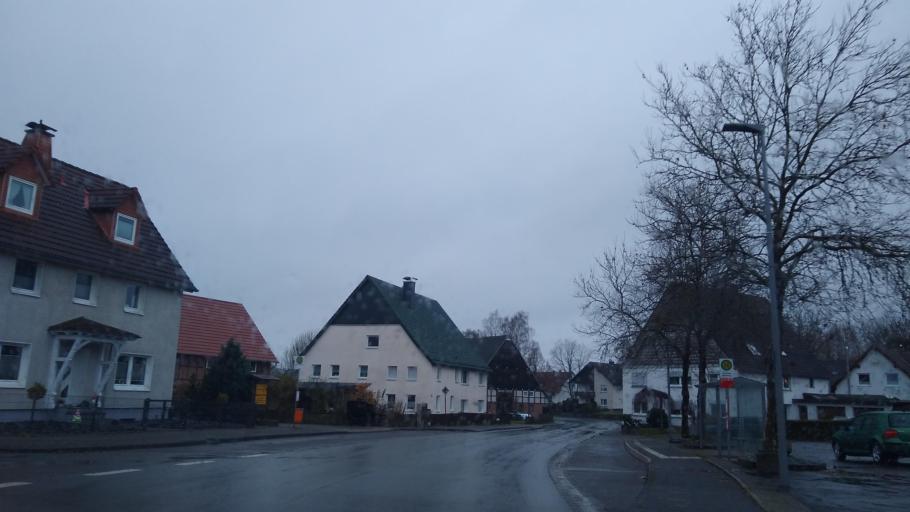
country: DE
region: Lower Saxony
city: Vahlbruch
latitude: 51.9125
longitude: 9.2879
